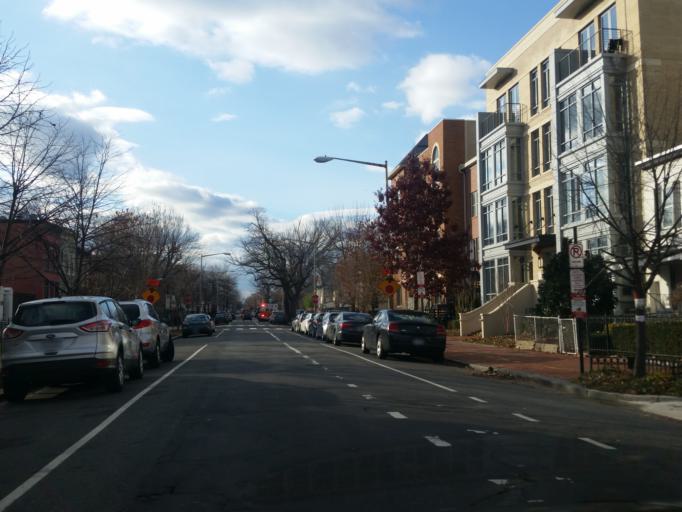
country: US
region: Washington, D.C.
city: Washington, D.C.
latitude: 38.9126
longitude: -77.0180
